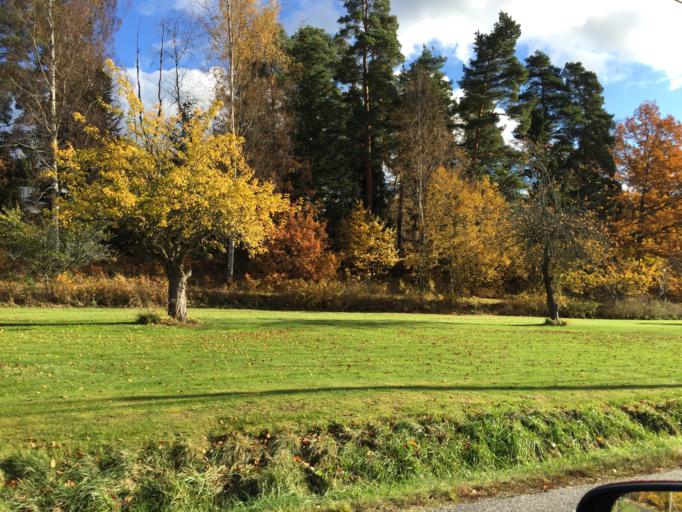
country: SE
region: Stockholm
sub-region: Salems Kommun
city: Ronninge
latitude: 59.1877
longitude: 17.7230
